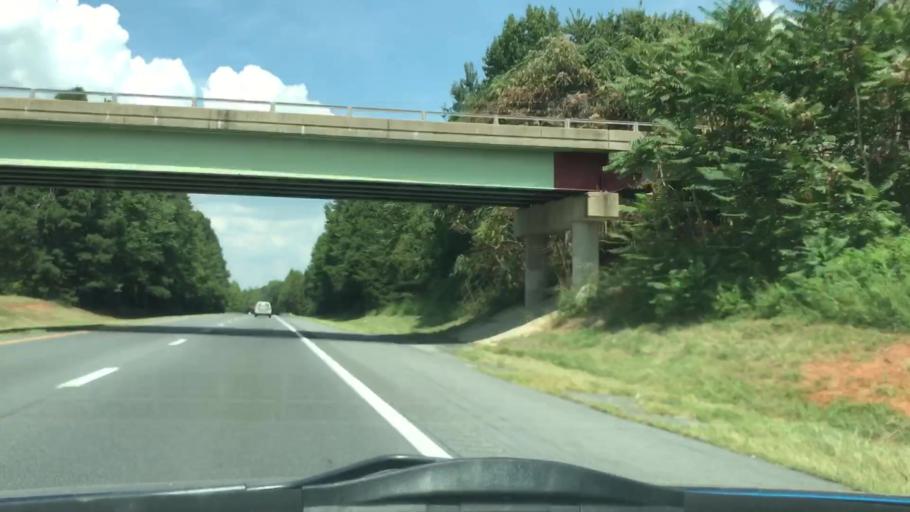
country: US
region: North Carolina
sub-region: Guilford County
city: Pleasant Garden
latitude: 35.9030
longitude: -79.8219
